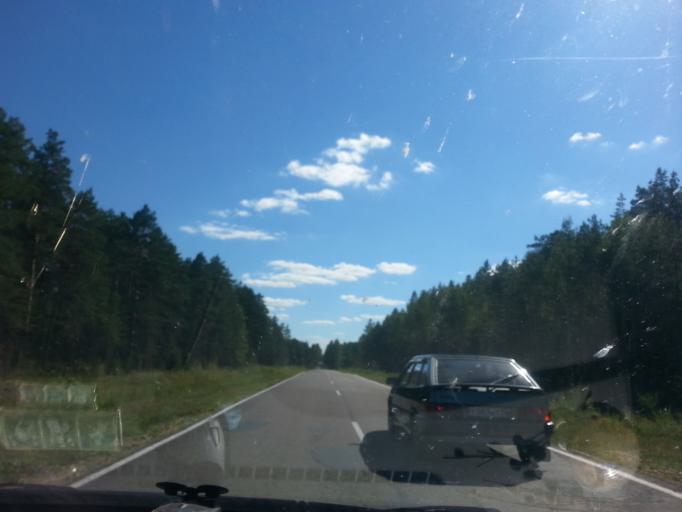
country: RU
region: Vladimir
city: Galitsy
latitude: 56.0407
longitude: 42.8629
